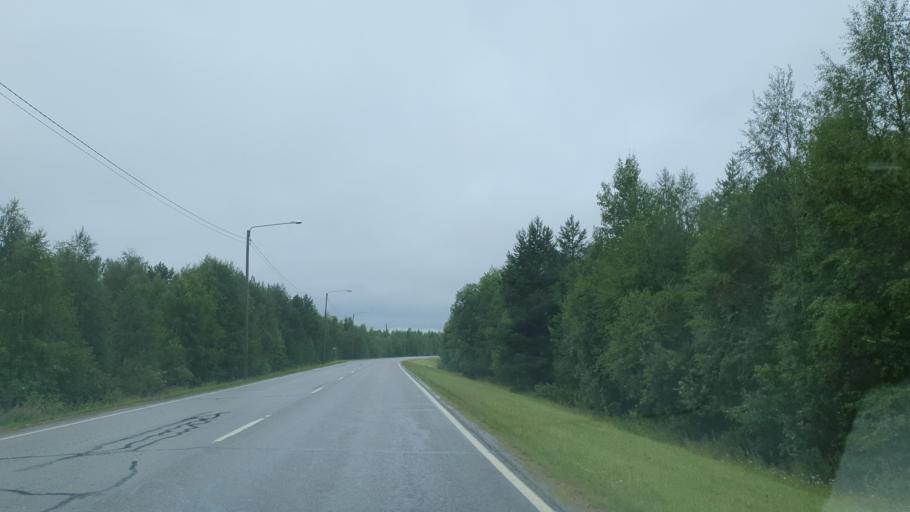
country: FI
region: Lapland
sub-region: Itae-Lappi
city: Kemijaervi
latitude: 66.6949
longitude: 27.5798
